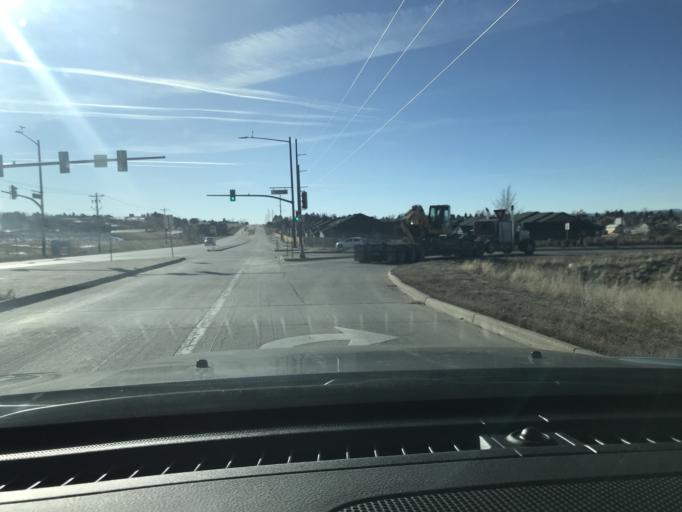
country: US
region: Colorado
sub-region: Douglas County
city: Parker
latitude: 39.5369
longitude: -104.7559
